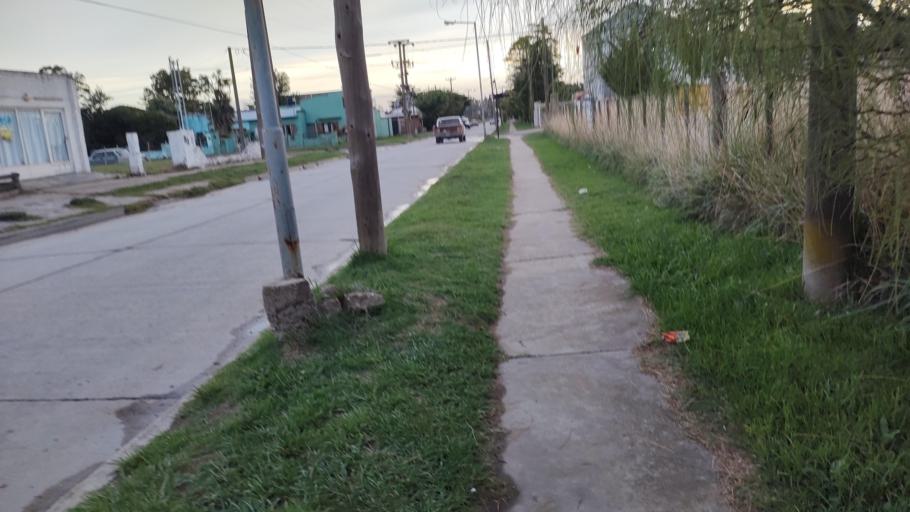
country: AR
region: Buenos Aires
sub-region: Partido de Loberia
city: Loberia
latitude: -38.1754
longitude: -58.7757
